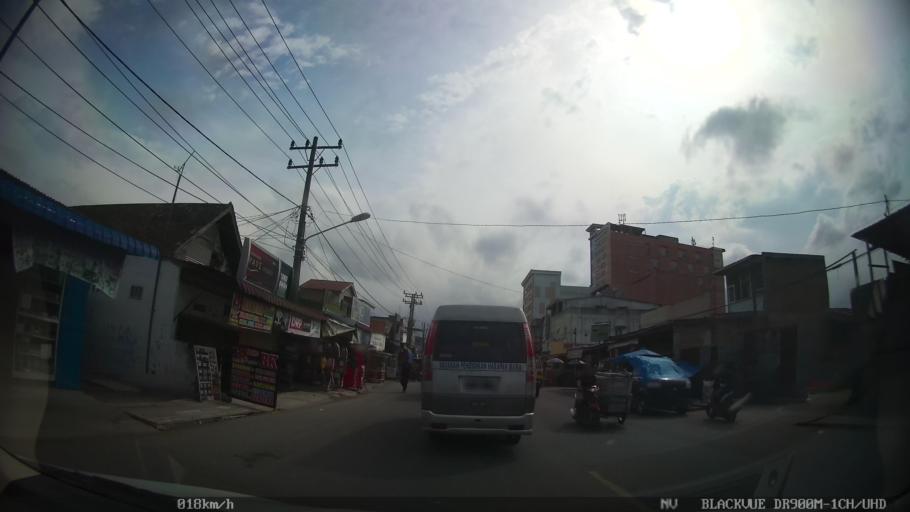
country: ID
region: North Sumatra
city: Medan
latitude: 3.5988
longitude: 98.7560
